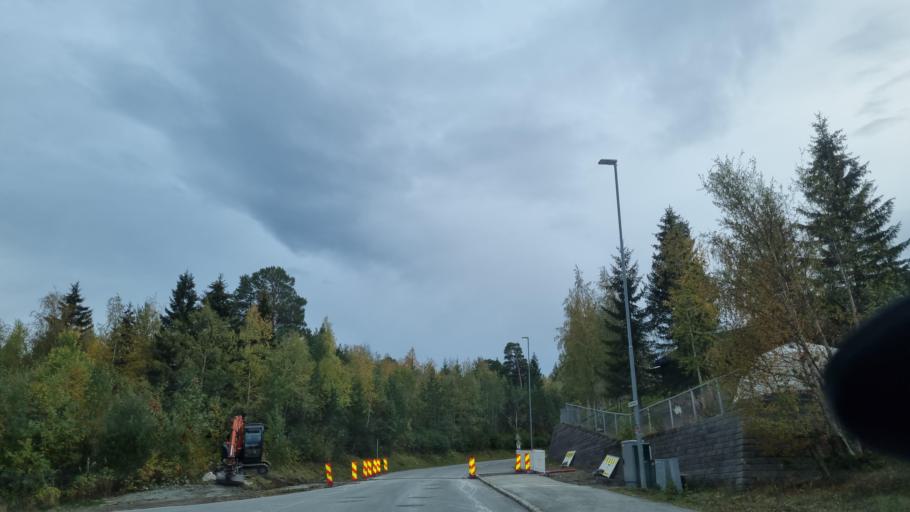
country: NO
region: Sor-Trondelag
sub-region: Malvik
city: Hommelvik
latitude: 63.4231
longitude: 10.7628
